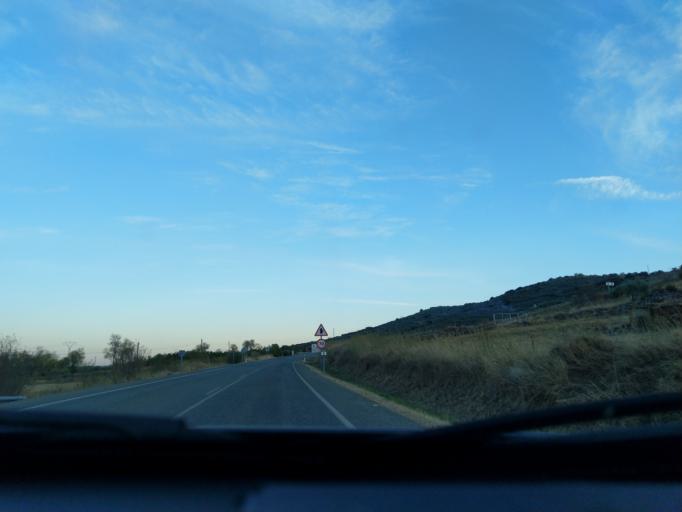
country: ES
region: Extremadura
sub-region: Provincia de Badajoz
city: Reina
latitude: 38.1908
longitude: -5.9467
